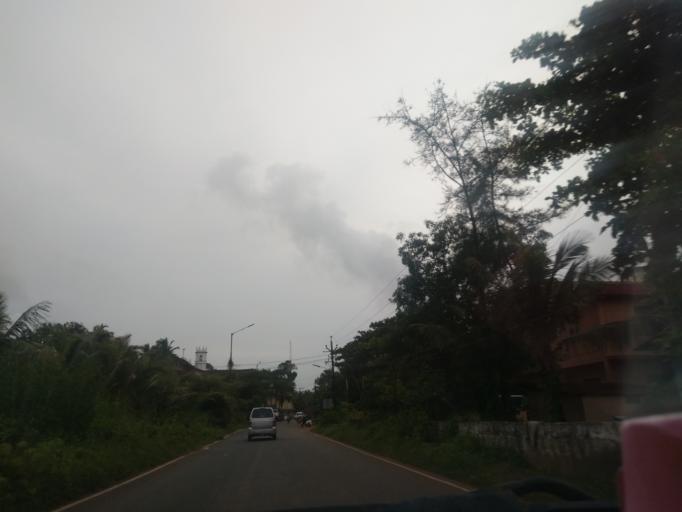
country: IN
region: Goa
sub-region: South Goa
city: Madgaon
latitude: 15.2582
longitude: 73.9682
